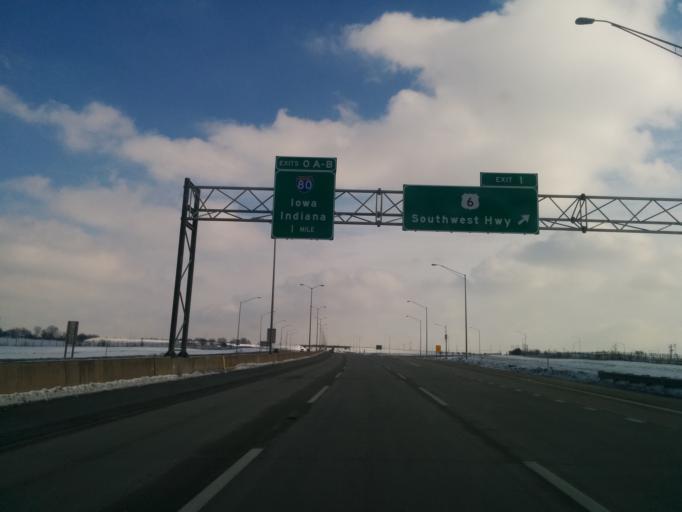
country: US
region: Illinois
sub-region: Will County
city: New Lenox
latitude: 41.5540
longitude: -87.9831
